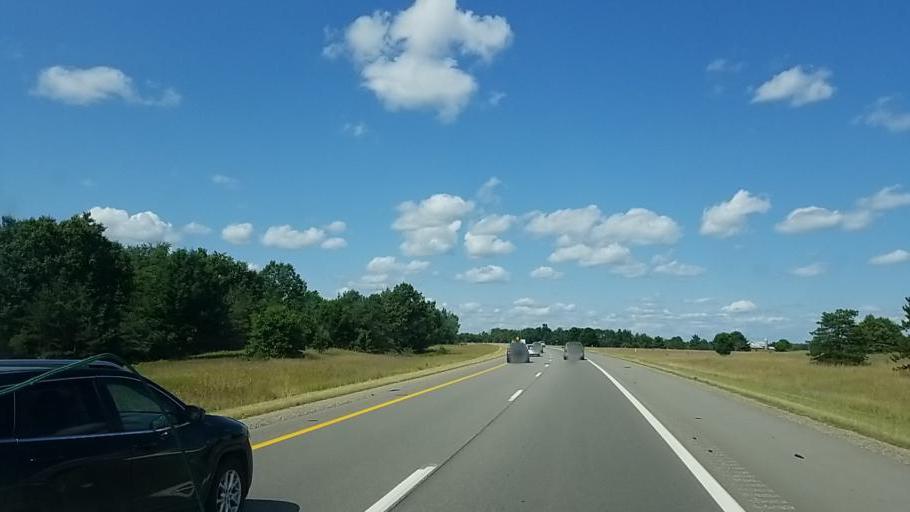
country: US
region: Michigan
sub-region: Montcalm County
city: Howard City
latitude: 43.4594
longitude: -85.4781
